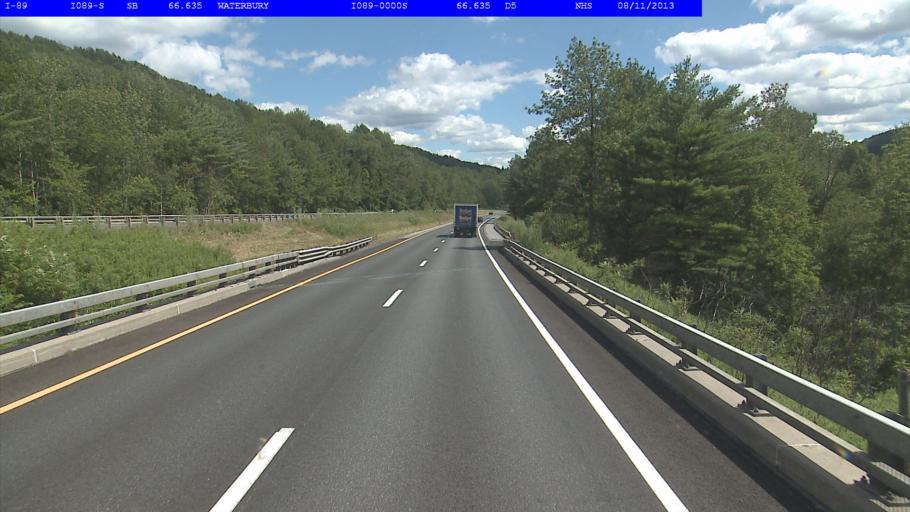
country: US
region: Vermont
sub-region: Washington County
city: Waterbury
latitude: 44.3610
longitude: -72.8030
